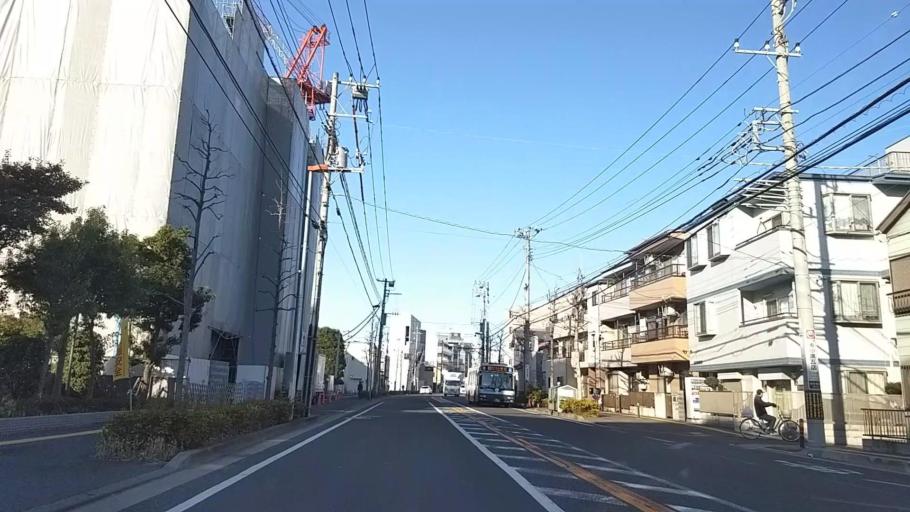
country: JP
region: Tokyo
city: Chofugaoka
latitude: 35.6003
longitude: 139.6238
